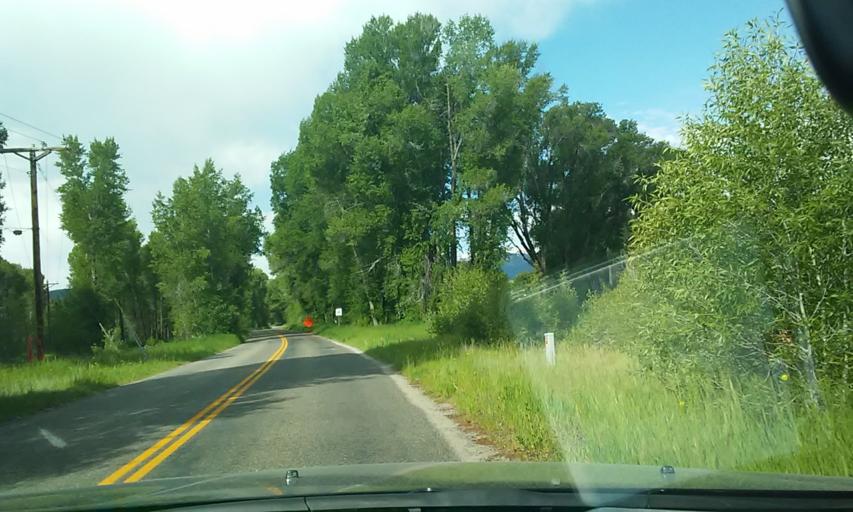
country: US
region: Wyoming
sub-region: Teton County
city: Jackson
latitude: 43.5616
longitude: -110.7572
